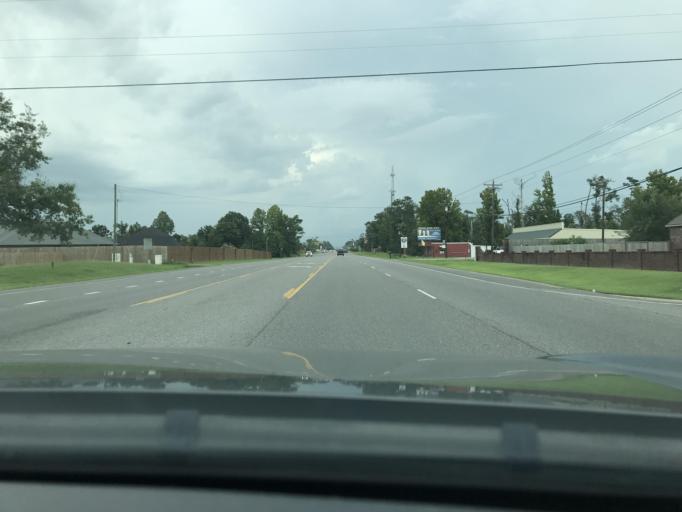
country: US
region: Louisiana
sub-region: Calcasieu Parish
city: Moss Bluff
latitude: 30.3008
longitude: -93.2421
